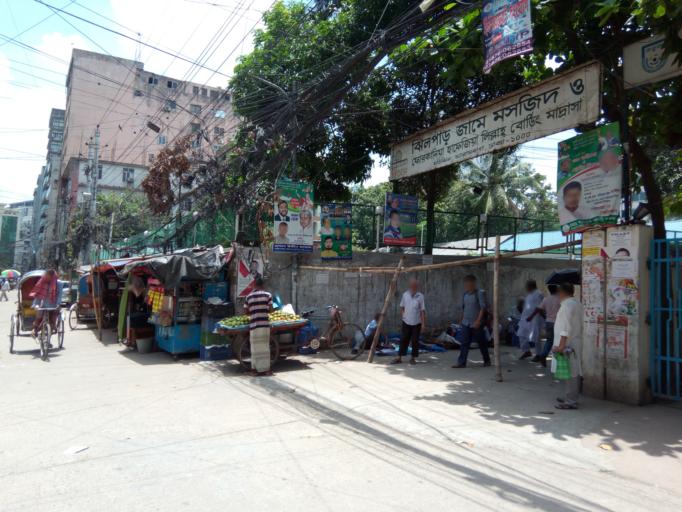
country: BD
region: Dhaka
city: Paltan
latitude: 23.7291
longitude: 90.4186
